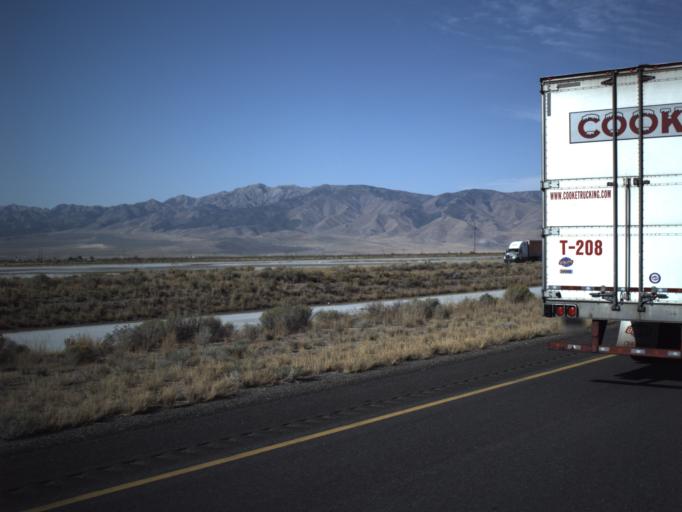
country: US
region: Utah
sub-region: Tooele County
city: Grantsville
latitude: 40.6811
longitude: -112.4226
